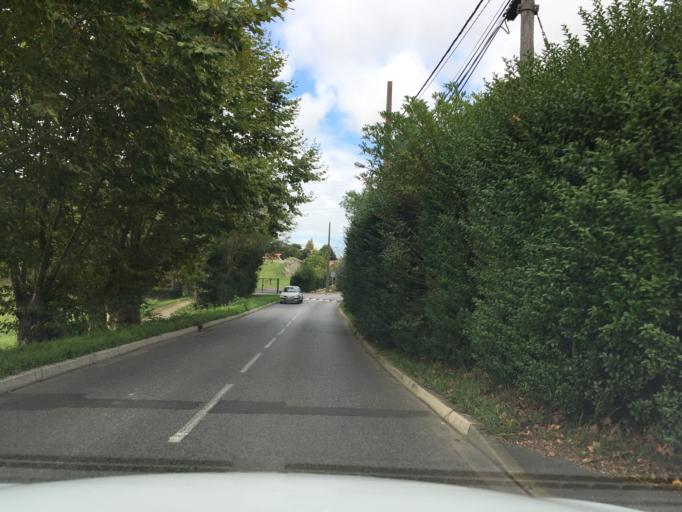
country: FR
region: Aquitaine
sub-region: Departement des Pyrenees-Atlantiques
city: Bassussarry
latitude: 43.4533
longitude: -1.4976
